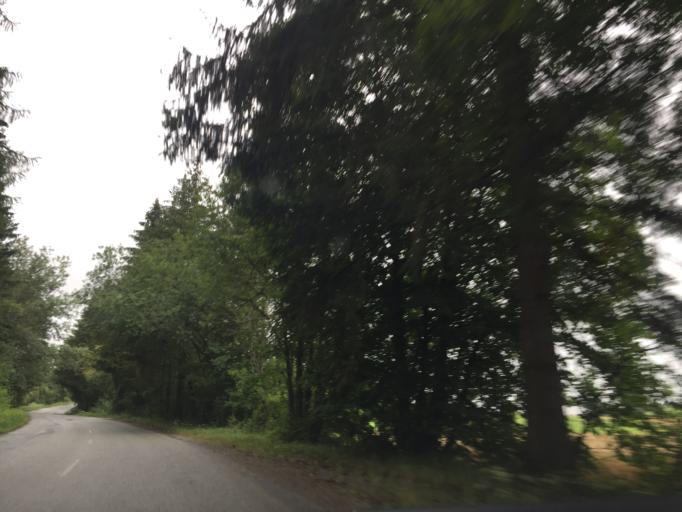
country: CZ
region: South Moravian
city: Ostrov u Macochy
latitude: 49.4003
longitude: 16.7629
